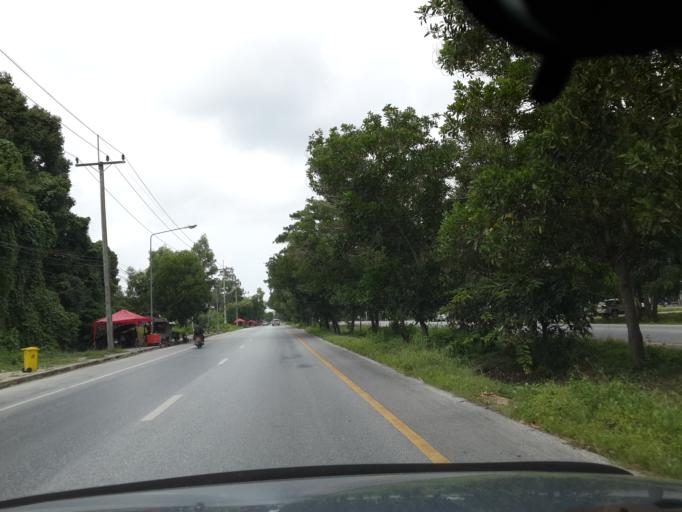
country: TH
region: Pattani
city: Yaring
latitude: 6.8627
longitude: 101.3659
